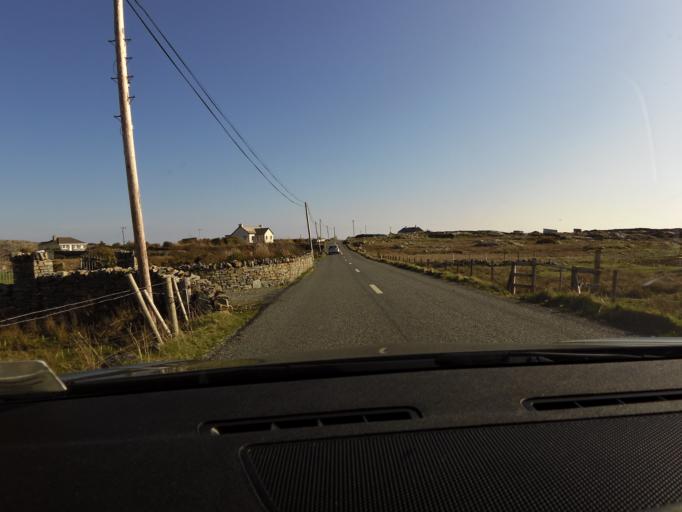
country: IE
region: Connaught
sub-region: County Galway
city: Clifden
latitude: 53.4053
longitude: -10.0328
